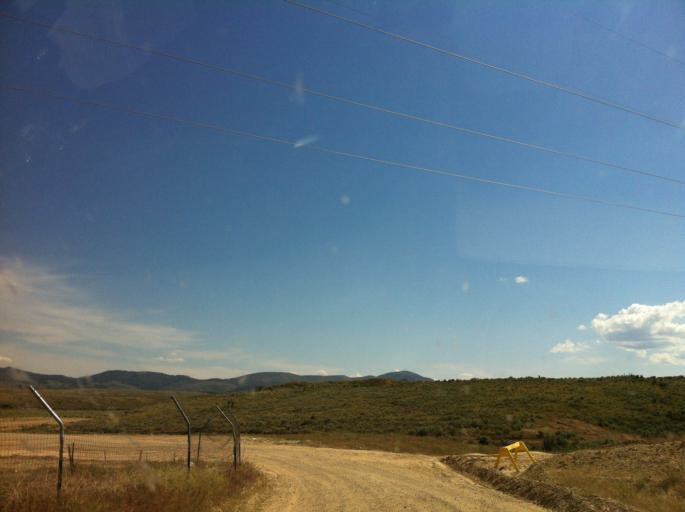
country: US
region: Oregon
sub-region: Baker County
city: Baker City
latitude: 44.7057
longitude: -117.7883
